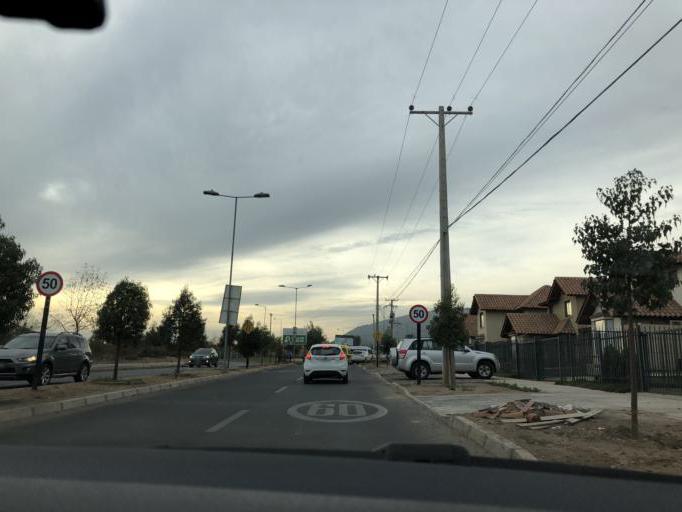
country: CL
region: Santiago Metropolitan
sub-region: Provincia de Cordillera
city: Puente Alto
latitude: -33.5907
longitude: -70.5082
